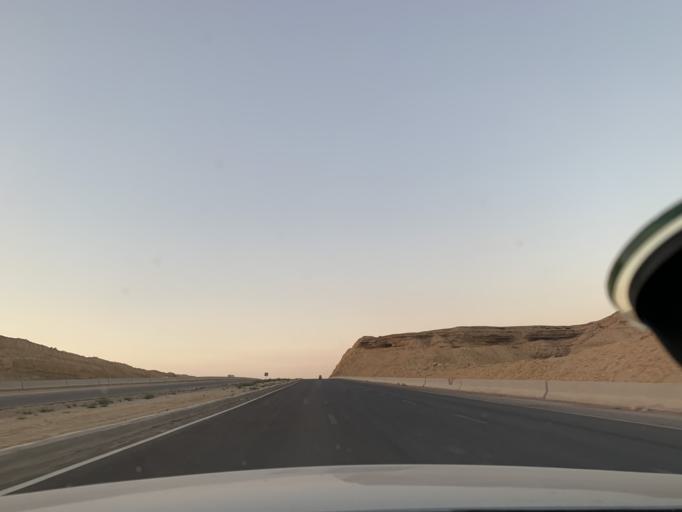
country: EG
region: Muhafazat al Qahirah
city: Halwan
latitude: 29.9483
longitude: 31.5368
